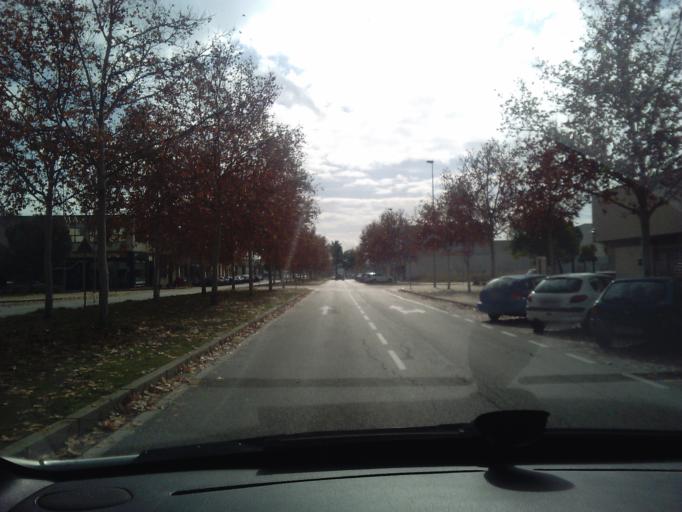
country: ES
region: Andalusia
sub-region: Provincia de Sevilla
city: Sevilla
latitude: 37.3780
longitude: -5.9193
